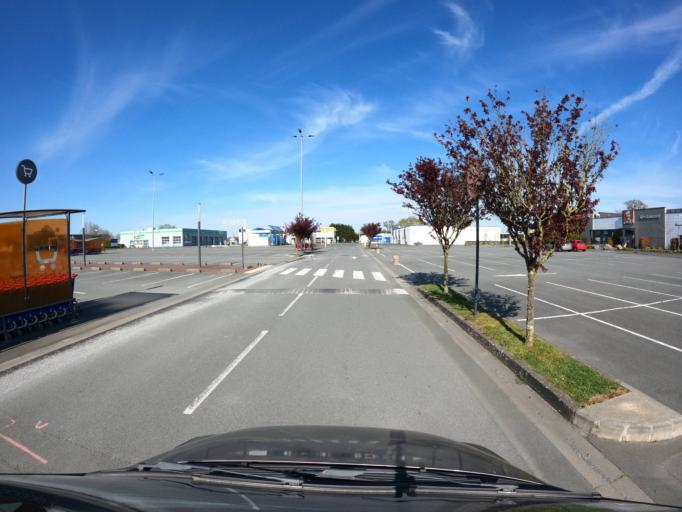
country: FR
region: Pays de la Loire
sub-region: Departement de Maine-et-Loire
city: Mazieres-en-Mauges
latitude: 47.0754
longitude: -0.8420
